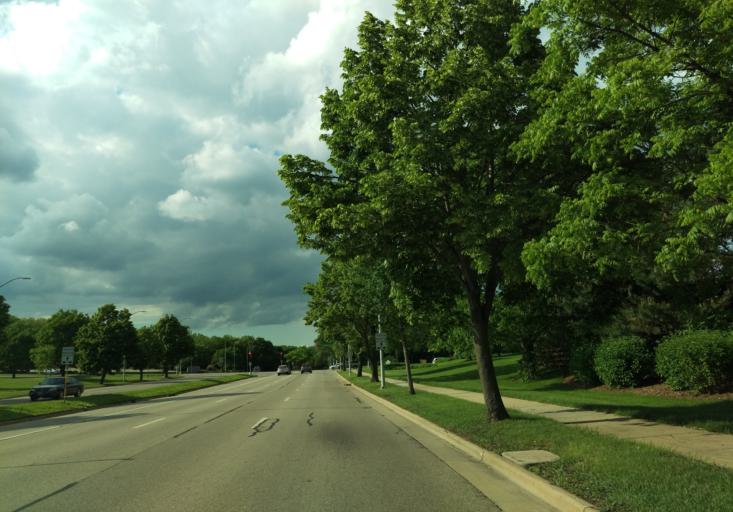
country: US
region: Wisconsin
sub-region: Dane County
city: Shorewood Hills
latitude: 43.0597
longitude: -89.4718
